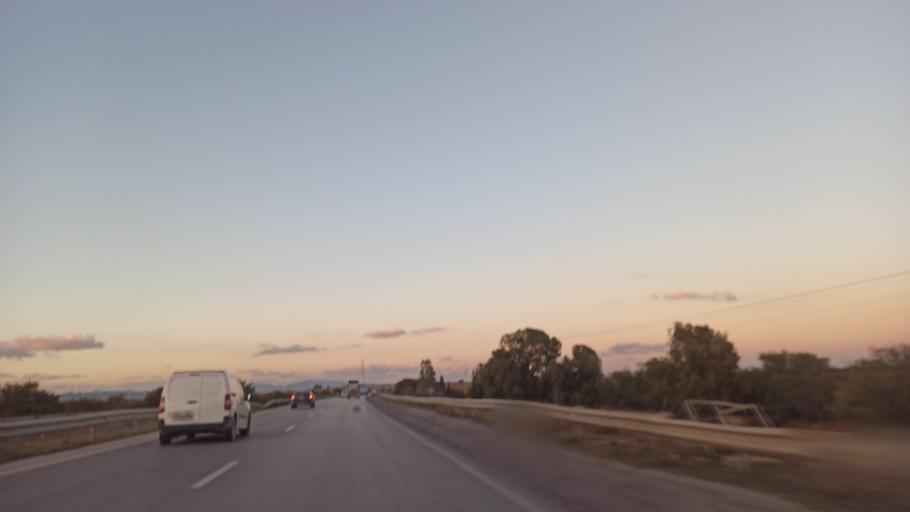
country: TN
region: Nabul
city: Al Hammamat
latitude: 36.2585
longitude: 10.4281
